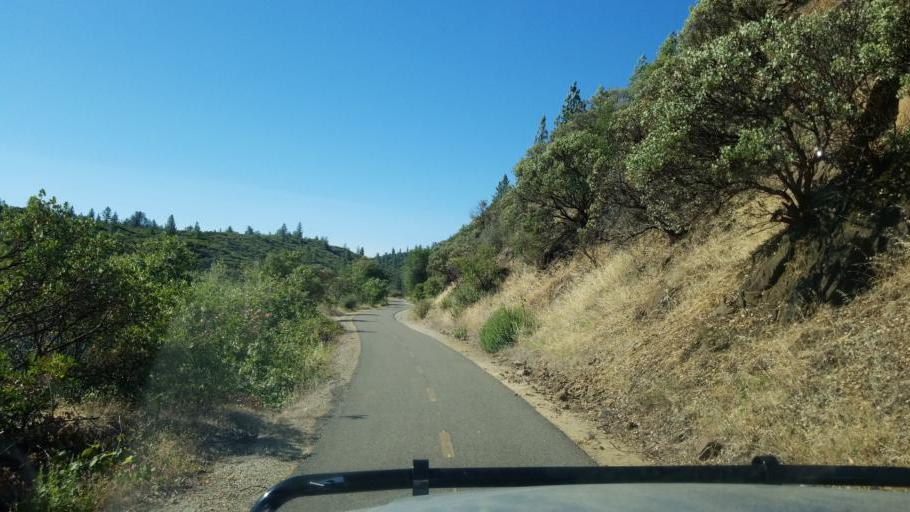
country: US
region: California
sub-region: Shasta County
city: Shasta
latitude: 40.6689
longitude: -122.4610
